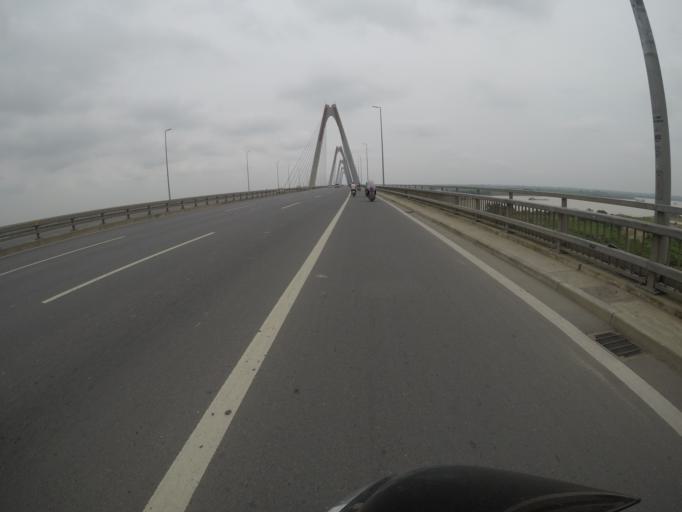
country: VN
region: Ha Noi
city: Tay Ho
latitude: 21.0868
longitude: 105.8180
